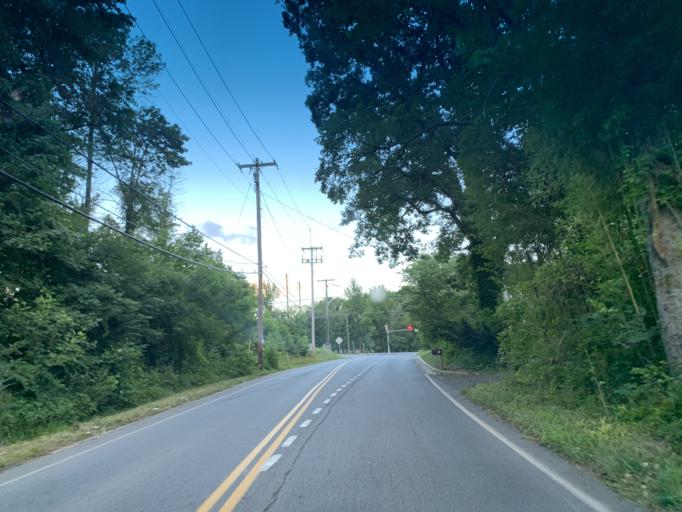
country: US
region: Maryland
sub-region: Harford County
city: Aberdeen
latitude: 39.5248
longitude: -76.1406
